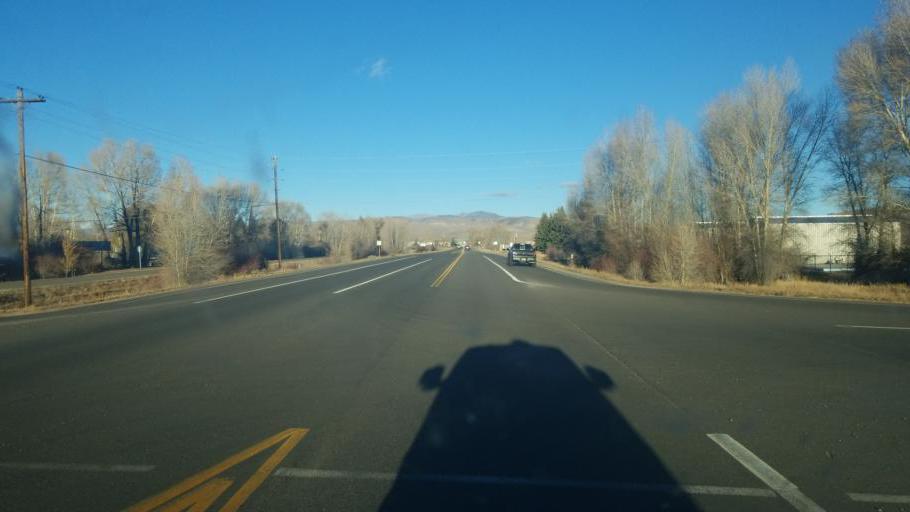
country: US
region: Colorado
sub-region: Gunnison County
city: Gunnison
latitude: 38.5347
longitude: -106.9481
